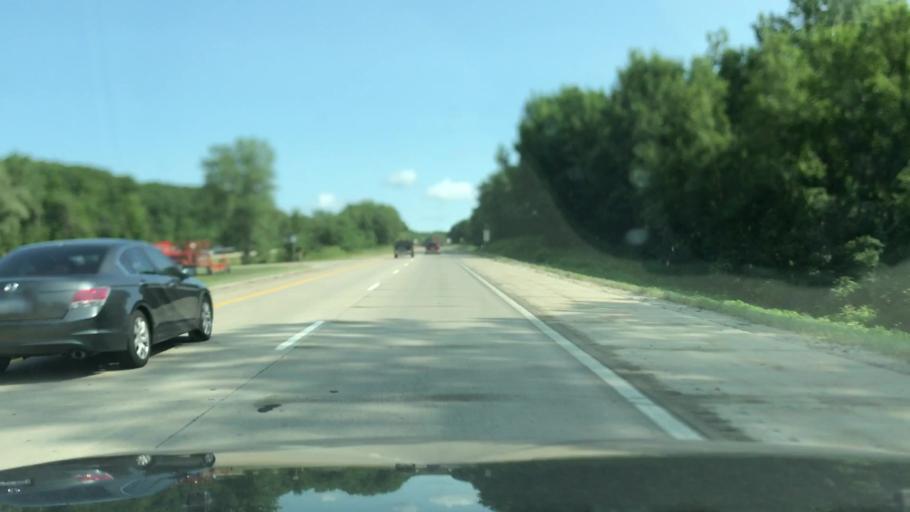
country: US
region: Michigan
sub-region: Kent County
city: Comstock Park
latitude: 43.0533
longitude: -85.6627
